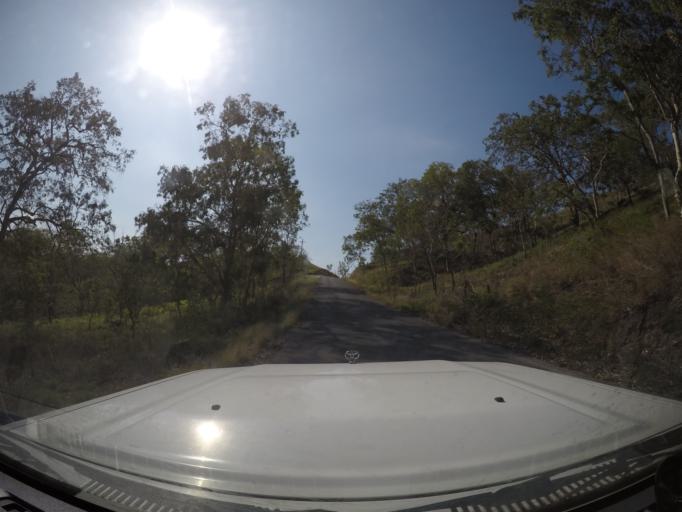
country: PG
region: Central Province
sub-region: Rigo
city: Kwikila
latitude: -9.8688
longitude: 147.5645
